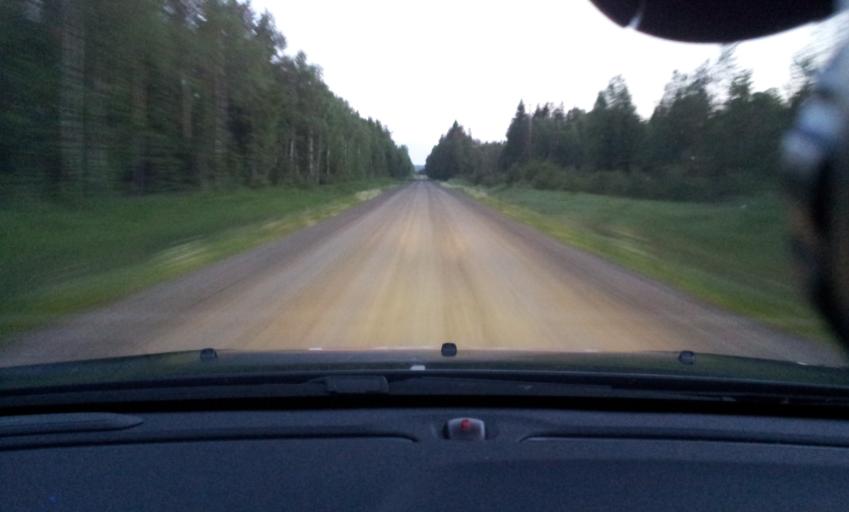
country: SE
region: Vaesternorrland
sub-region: Ange Kommun
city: Ange
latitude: 62.7572
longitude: 15.6651
